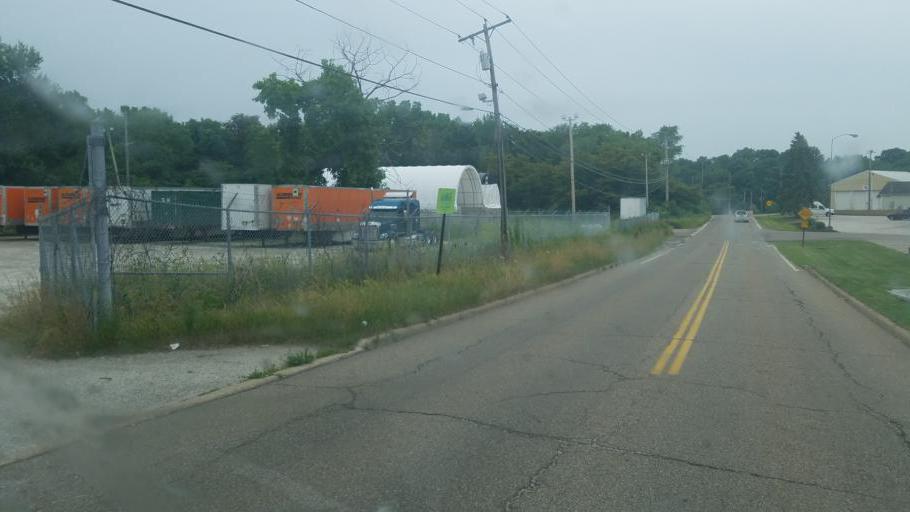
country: US
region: Ohio
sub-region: Summit County
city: Mogadore
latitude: 41.0590
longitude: -81.4221
